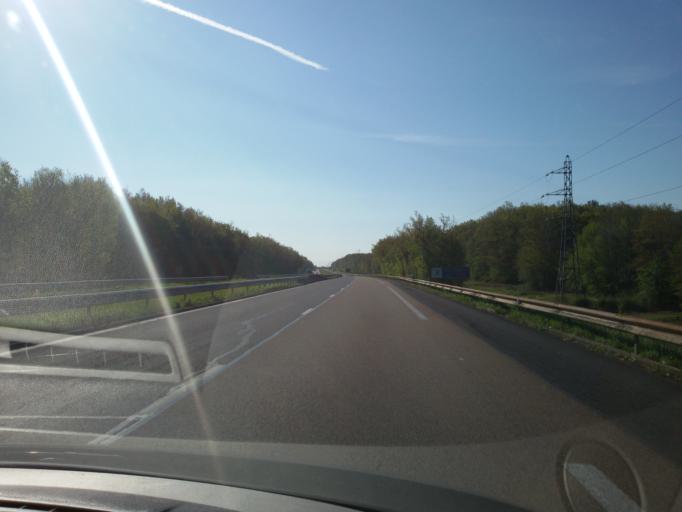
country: FR
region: Centre
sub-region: Departement du Loiret
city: Courtenay
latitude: 48.0833
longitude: 3.0479
